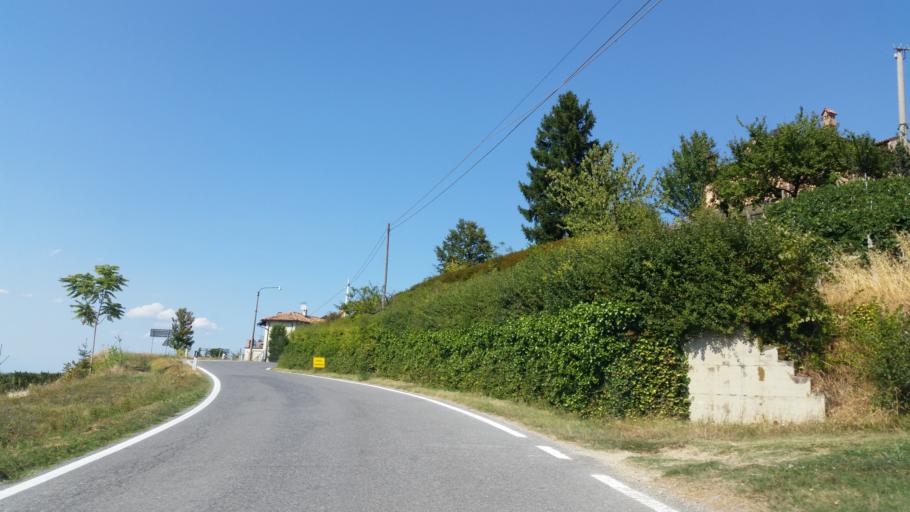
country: IT
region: Piedmont
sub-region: Provincia di Cuneo
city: Serralunga d'Alba
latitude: 44.6059
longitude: 7.9996
